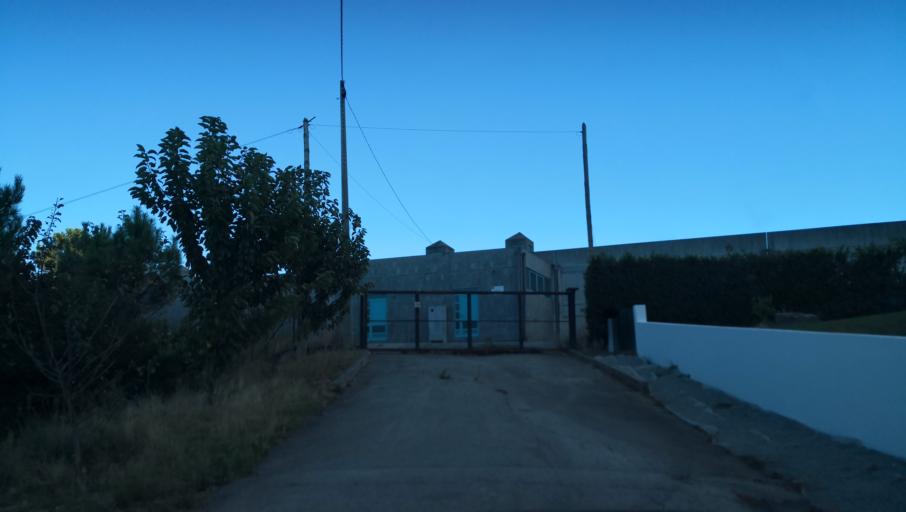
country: PT
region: Vila Real
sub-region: Vila Real
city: Vila Real
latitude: 41.2806
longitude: -7.7632
